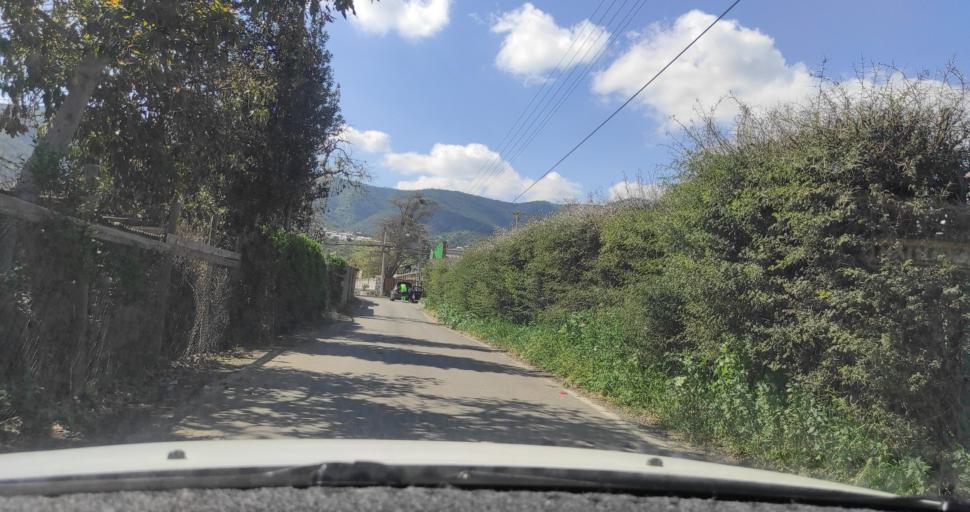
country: CL
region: Valparaiso
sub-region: Provincia de Marga Marga
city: Limache
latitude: -32.9961
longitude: -71.2325
